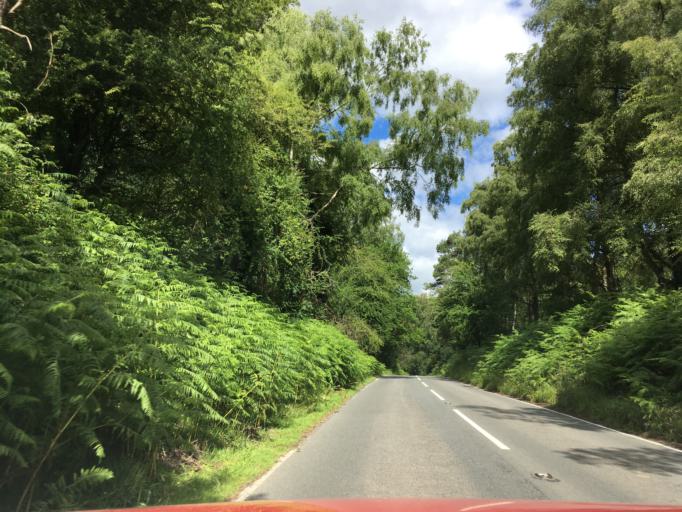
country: GB
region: England
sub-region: Gloucestershire
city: Lydney
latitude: 51.7759
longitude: -2.5228
